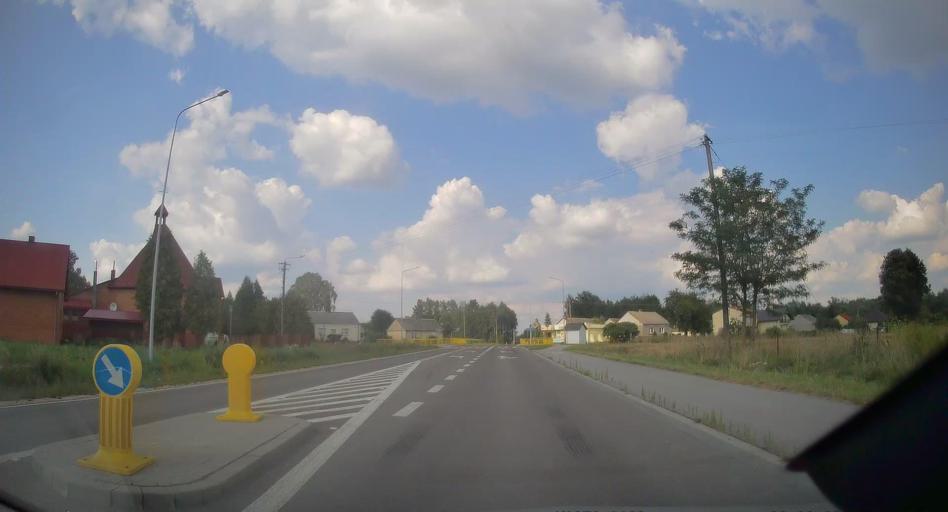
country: PL
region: Swietokrzyskie
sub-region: Powiat kielecki
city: Lopuszno
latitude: 50.9865
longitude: 20.2562
